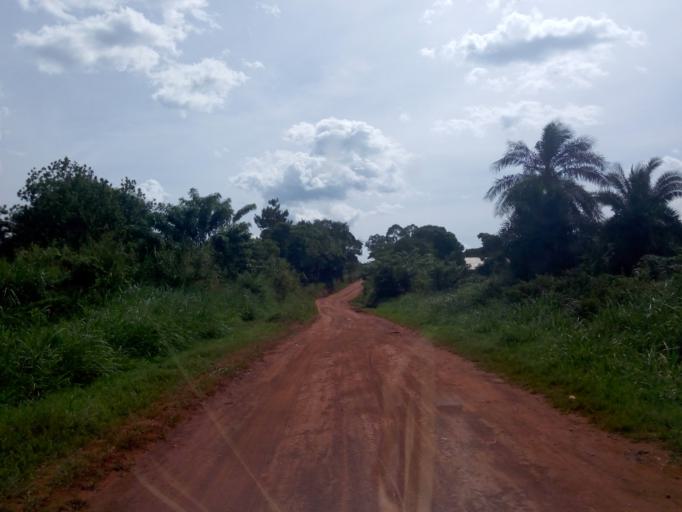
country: UG
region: Western Region
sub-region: Masindi District
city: Masindi
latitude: 1.6842
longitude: 31.7111
